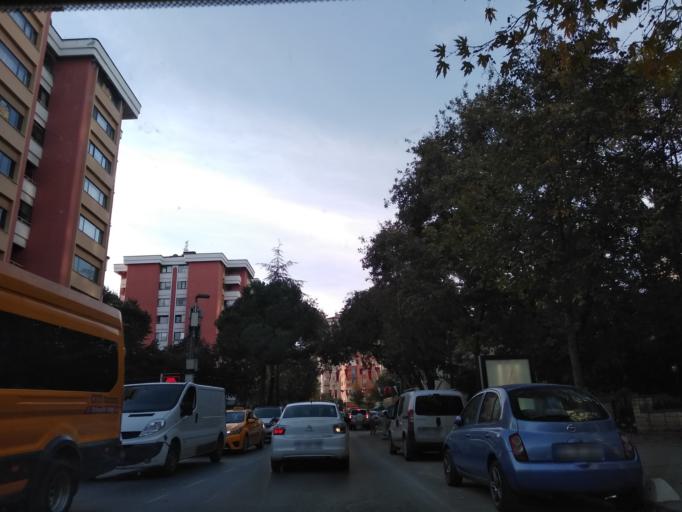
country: TR
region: Istanbul
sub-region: Atasehir
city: Atasehir
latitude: 40.9744
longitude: 29.0932
